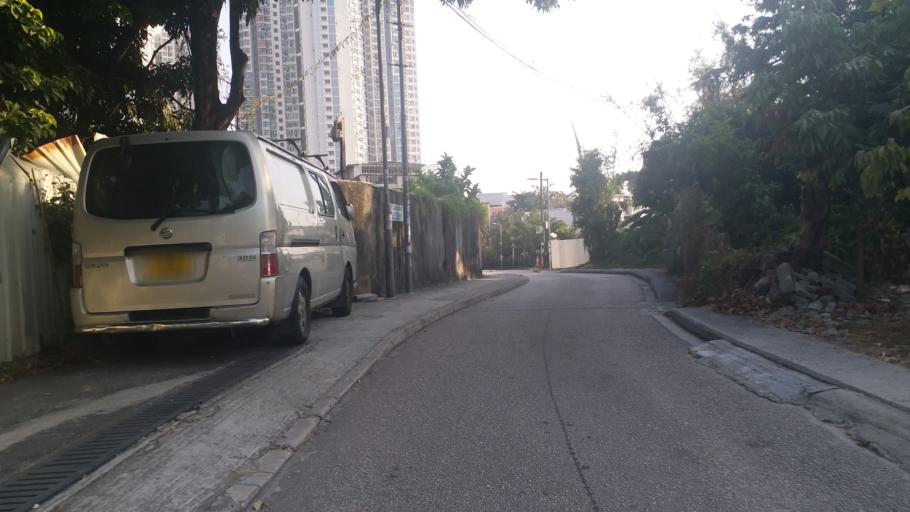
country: HK
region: Tuen Mun
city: Tuen Mun
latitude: 22.4166
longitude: 113.9739
